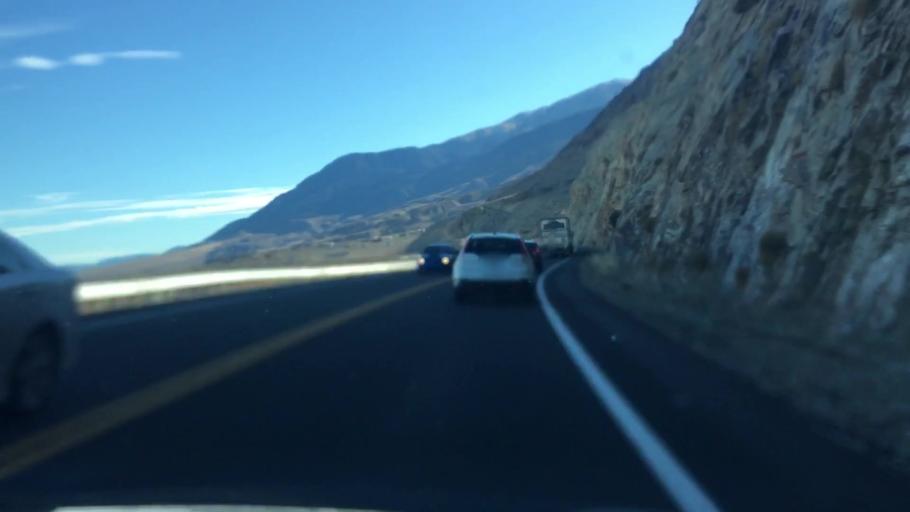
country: US
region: Nevada
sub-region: Mineral County
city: Hawthorne
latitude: 38.6678
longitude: -118.7674
